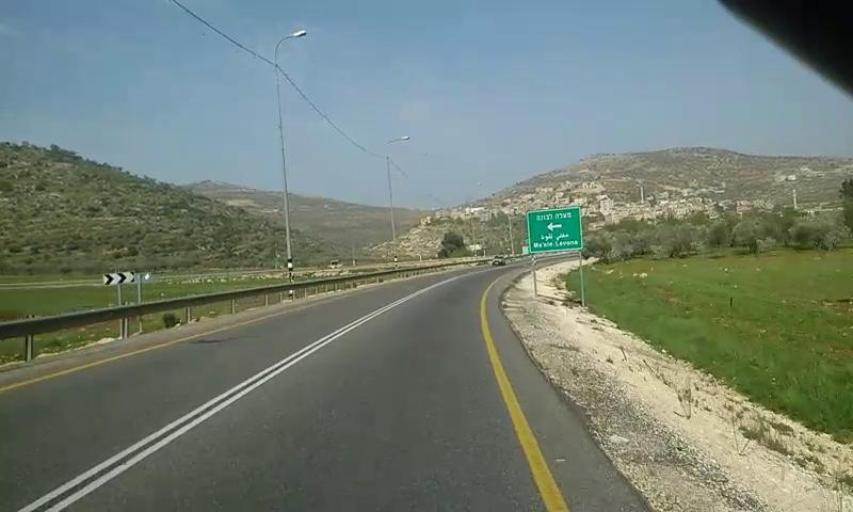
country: PS
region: West Bank
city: Al Lubban ash Sharqiyah
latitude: 32.0680
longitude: 35.2459
